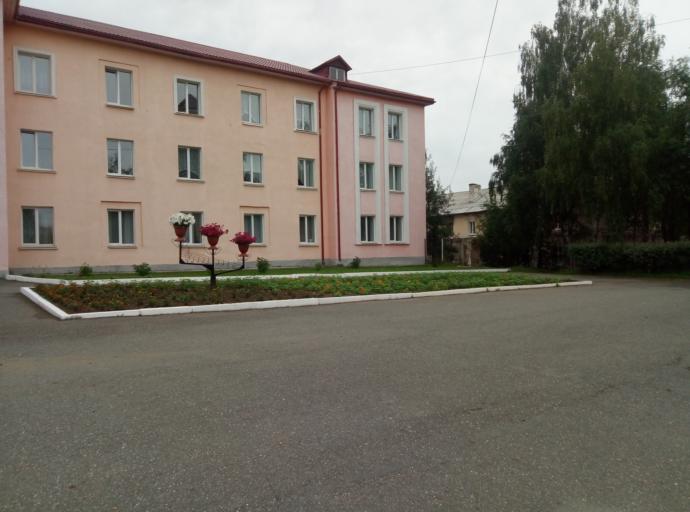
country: RU
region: Sverdlovsk
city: Krasnotur'insk
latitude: 59.7611
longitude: 60.1806
